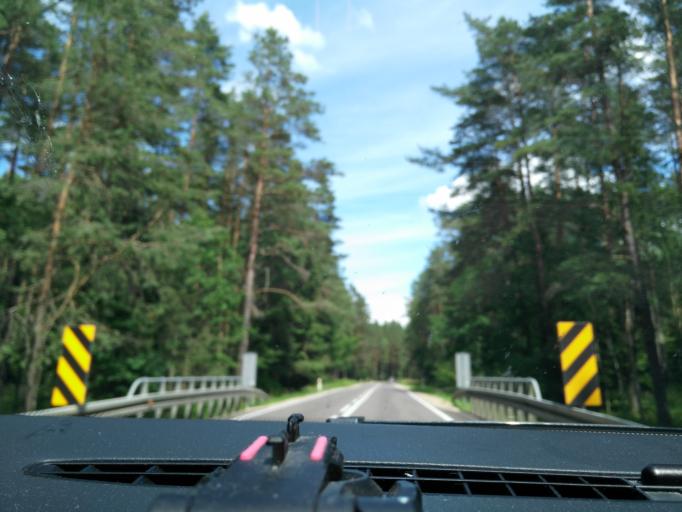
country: PL
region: Podlasie
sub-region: Powiat sejnenski
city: Krasnopol
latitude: 53.9730
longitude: 23.2603
